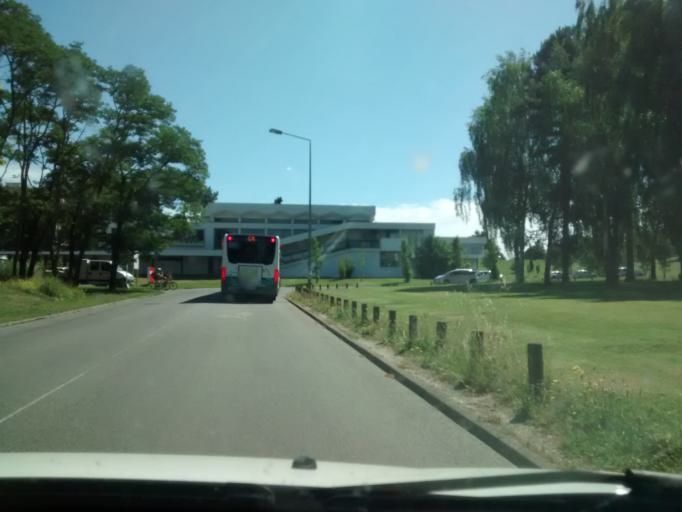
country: FR
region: Brittany
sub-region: Departement d'Ille-et-Vilaine
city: Cesson-Sevigne
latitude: 48.1201
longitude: -1.6366
